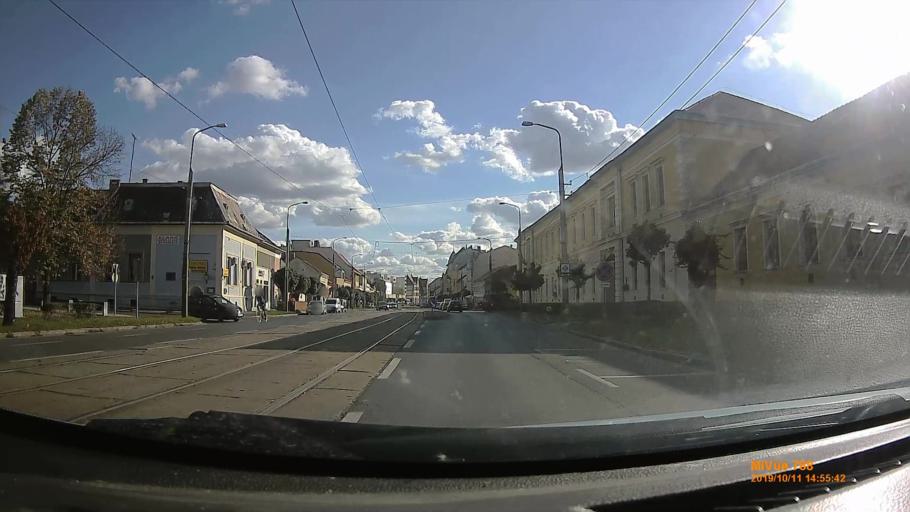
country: HU
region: Hajdu-Bihar
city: Debrecen
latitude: 47.5393
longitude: 21.6252
